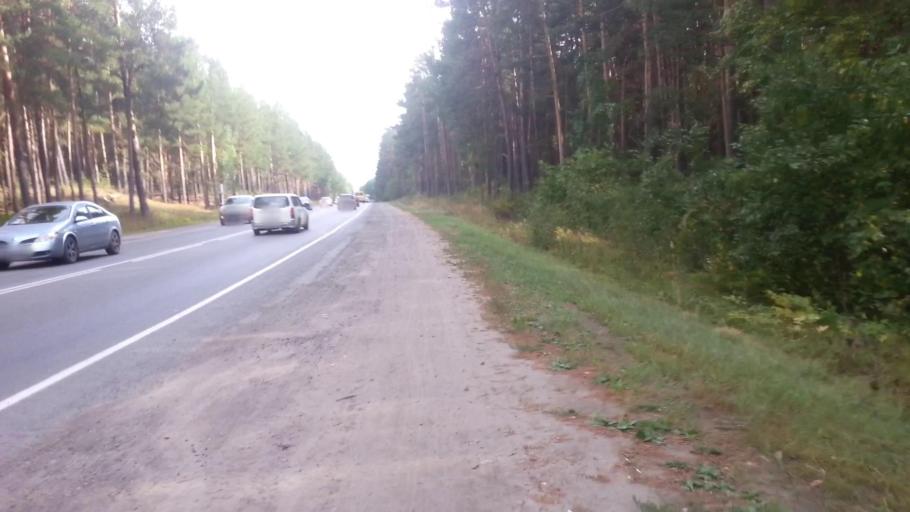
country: RU
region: Altai Krai
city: Yuzhnyy
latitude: 53.2976
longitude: 83.7032
